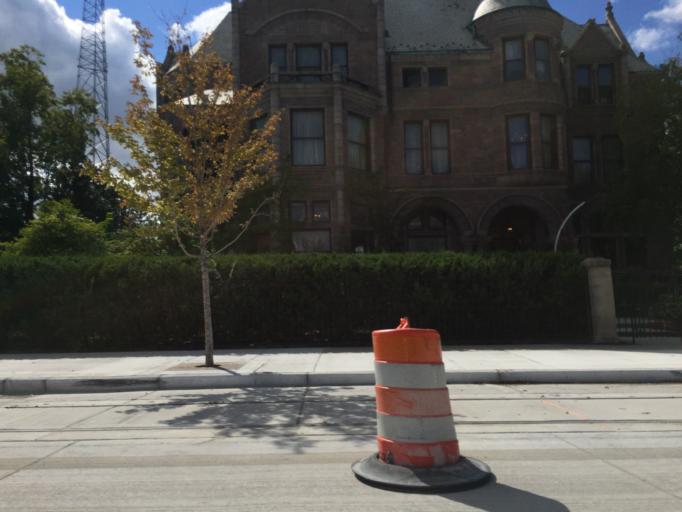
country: US
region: Michigan
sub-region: Wayne County
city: Detroit
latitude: 42.3530
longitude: -83.0618
